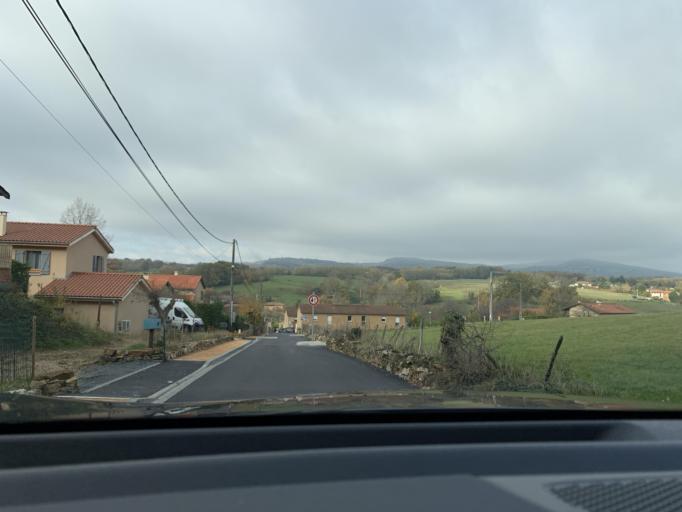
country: FR
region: Rhone-Alpes
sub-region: Departement du Rhone
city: Charnay
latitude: 45.9094
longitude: 4.6544
